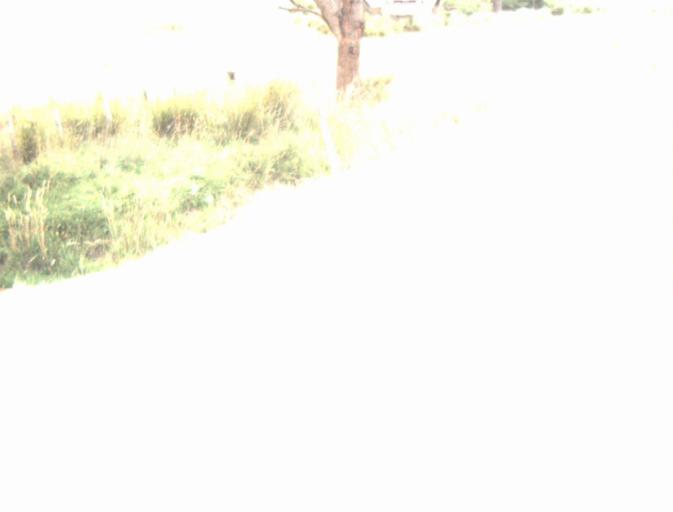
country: AU
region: Tasmania
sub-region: Dorset
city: Scottsdale
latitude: -41.4686
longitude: 147.5733
